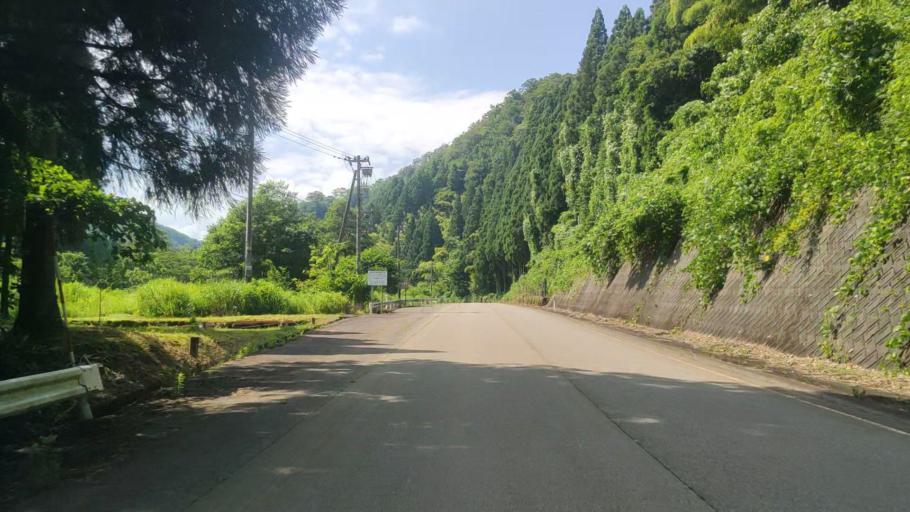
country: JP
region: Ishikawa
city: Komatsu
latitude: 36.3268
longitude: 136.5289
